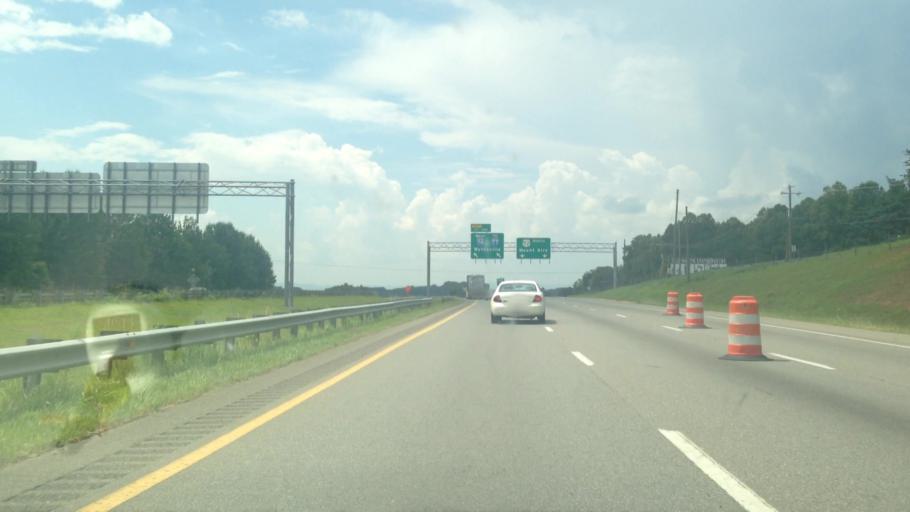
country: US
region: North Carolina
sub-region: Surry County
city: Flat Rock
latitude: 36.4448
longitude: -80.5432
